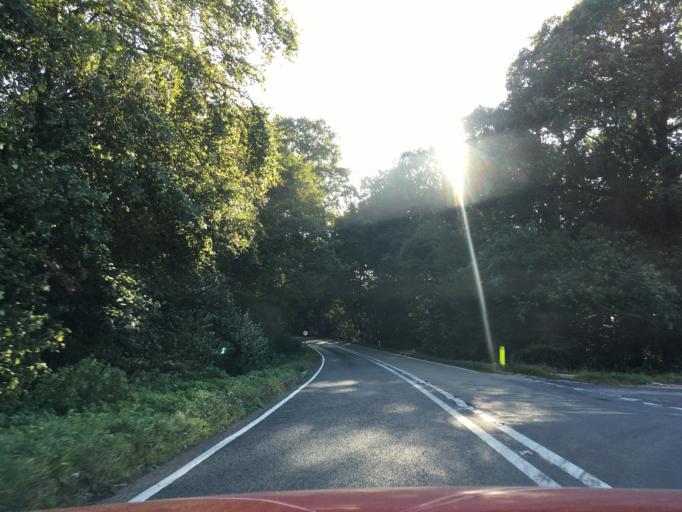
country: GB
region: England
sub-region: Hampshire
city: Swanmore
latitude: 50.9220
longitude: -1.1617
